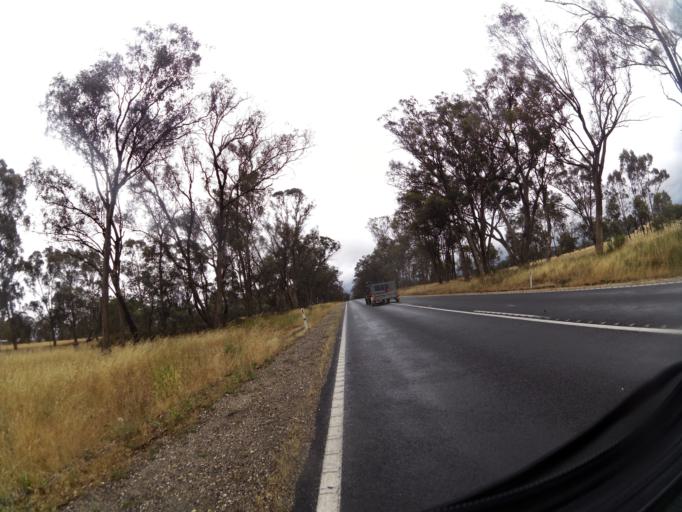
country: AU
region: Victoria
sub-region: Mount Alexander
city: Castlemaine
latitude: -37.0907
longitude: 144.1443
